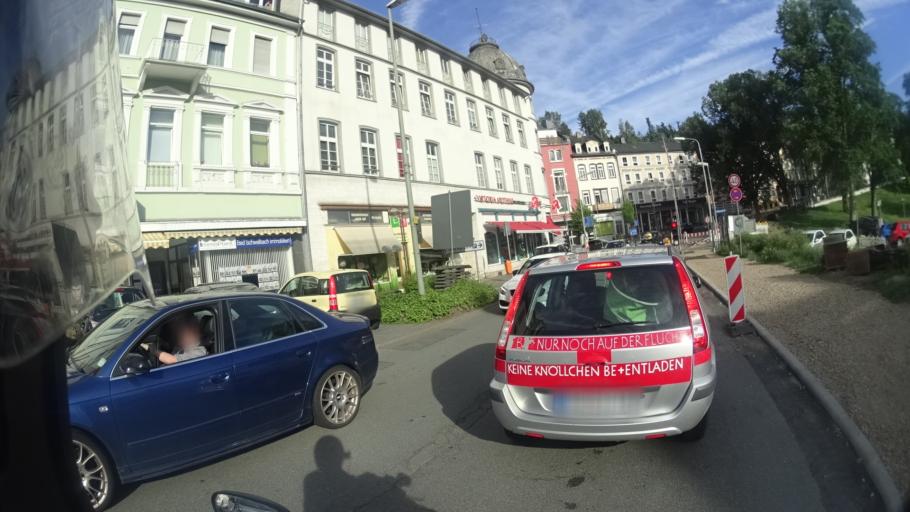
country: DE
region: Hesse
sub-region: Regierungsbezirk Darmstadt
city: Bad Schwalbach
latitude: 50.1389
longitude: 8.0688
